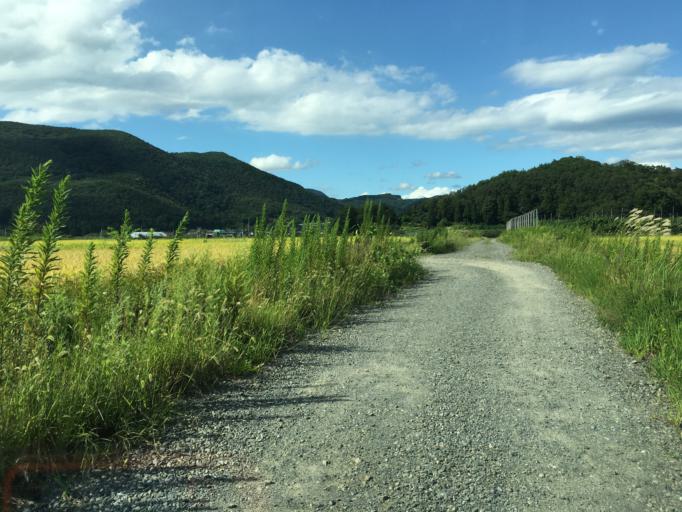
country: JP
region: Fukushima
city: Fukushima-shi
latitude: 37.8027
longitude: 140.4169
